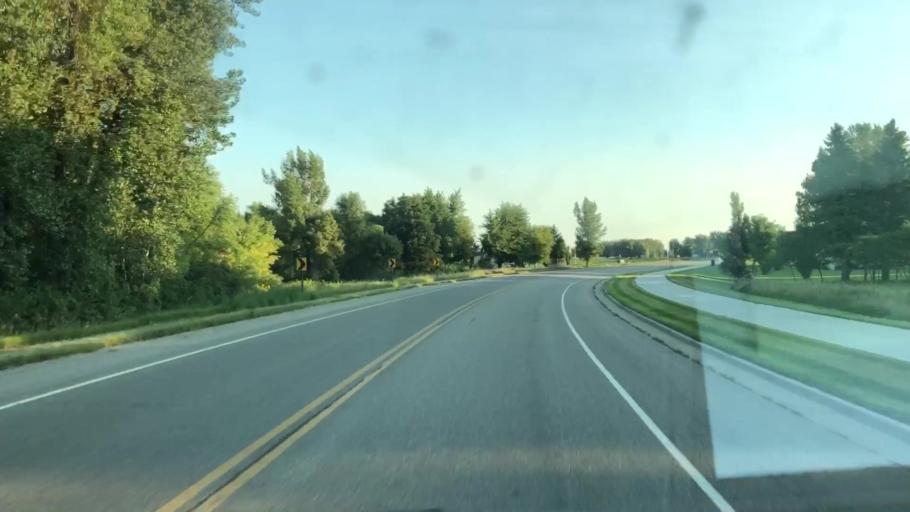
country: US
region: Minnesota
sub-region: Nobles County
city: Worthington
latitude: 43.6142
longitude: -95.6366
